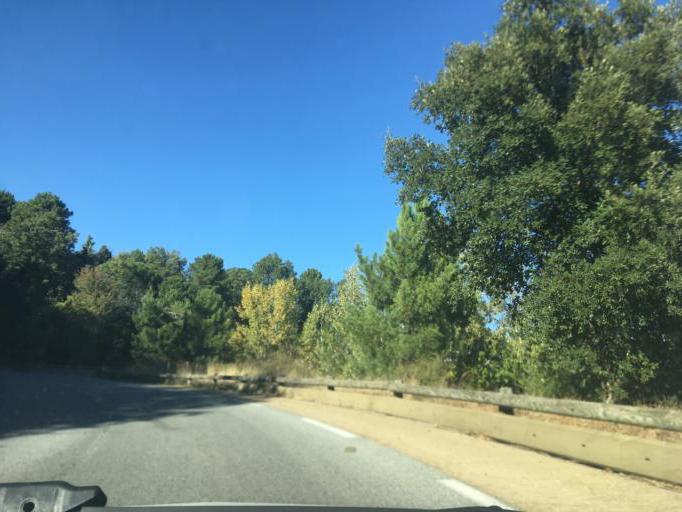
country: FR
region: Provence-Alpes-Cote d'Azur
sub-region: Departement du Var
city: La Garde-Freinet
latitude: 43.2998
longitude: 6.4752
